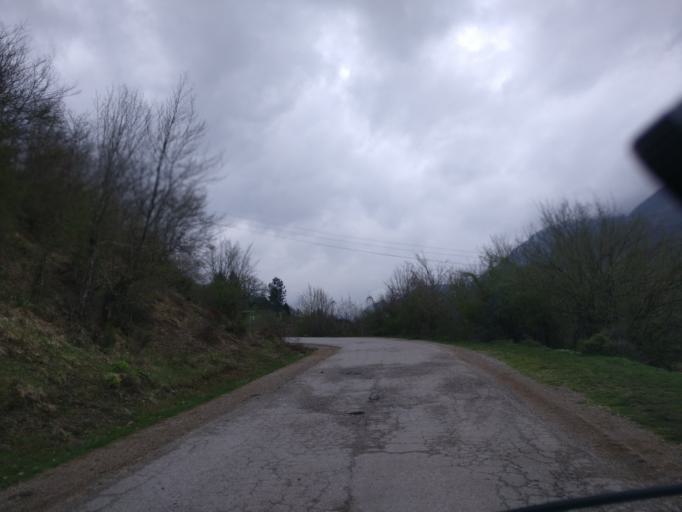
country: BA
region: Republika Srpska
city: Foca
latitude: 43.4391
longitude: 18.7630
